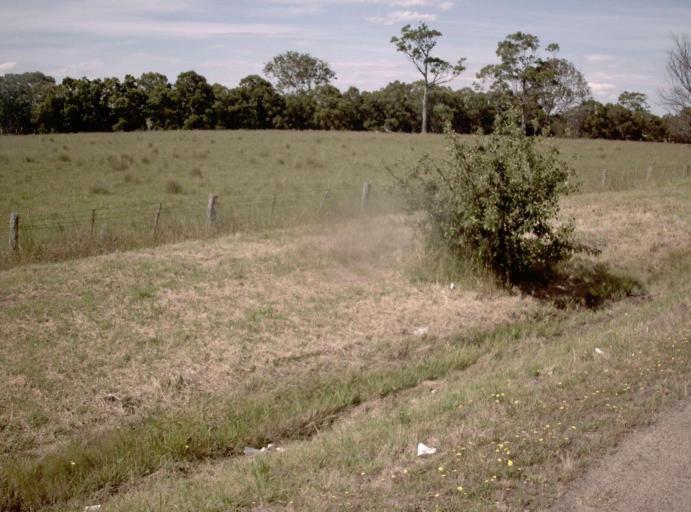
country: AU
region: Victoria
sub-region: East Gippsland
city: Bairnsdale
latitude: -37.8207
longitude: 147.7265
